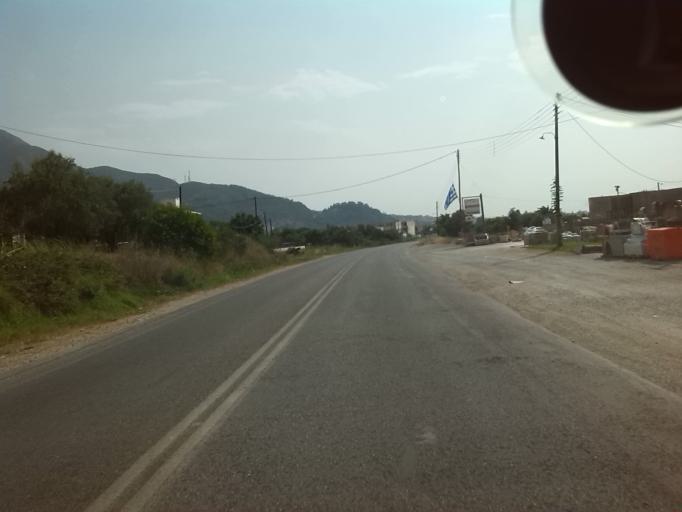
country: GR
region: Peloponnese
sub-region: Nomos Messinias
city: Kyparissia
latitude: 37.2697
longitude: 21.6945
